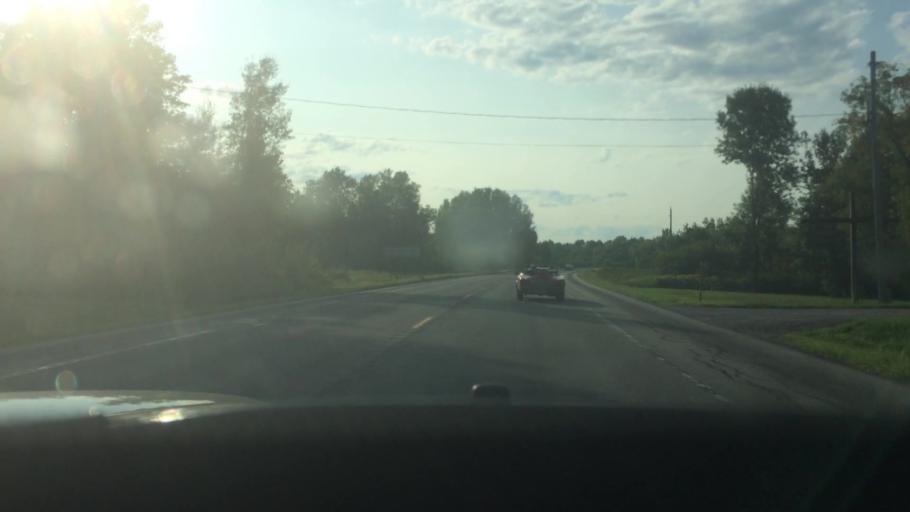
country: US
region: New York
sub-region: St. Lawrence County
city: Canton
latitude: 44.6200
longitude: -75.2267
